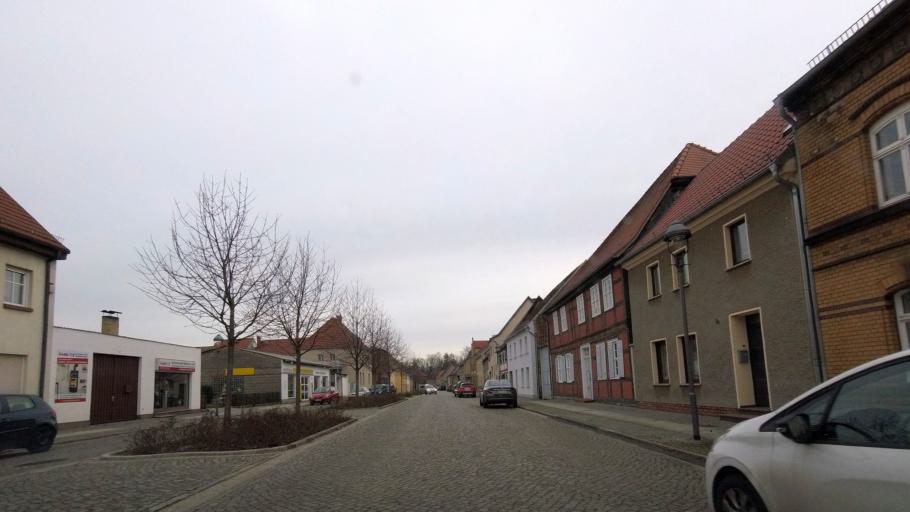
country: DE
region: Brandenburg
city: Treuenbrietzen
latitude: 52.0961
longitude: 12.8736
